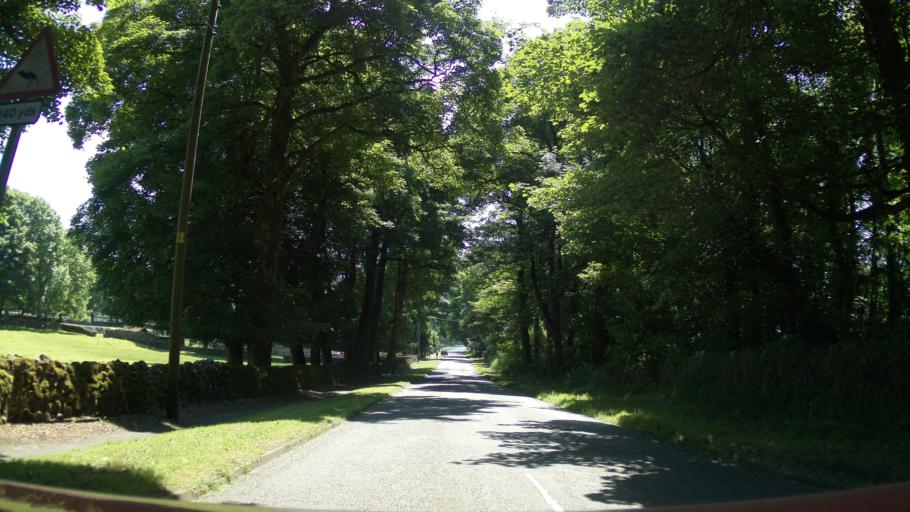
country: GB
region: England
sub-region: Derbyshire
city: Tideswell
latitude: 53.2693
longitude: -1.8188
